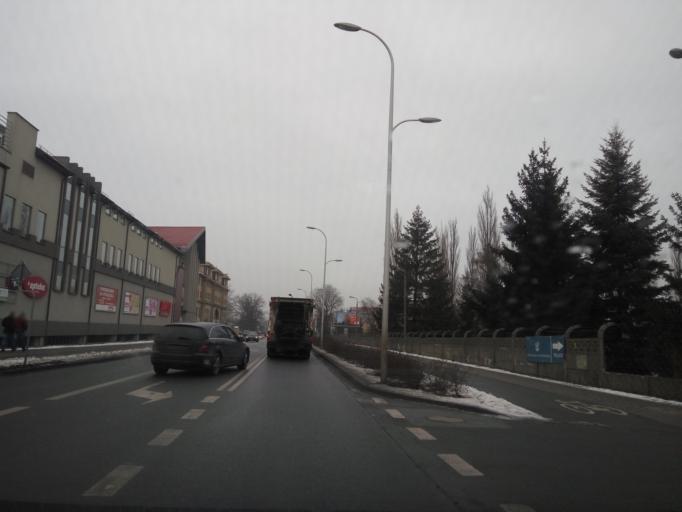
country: PL
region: Lower Silesian Voivodeship
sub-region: Powiat wroclawski
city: Wroclaw
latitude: 51.0592
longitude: 17.0101
